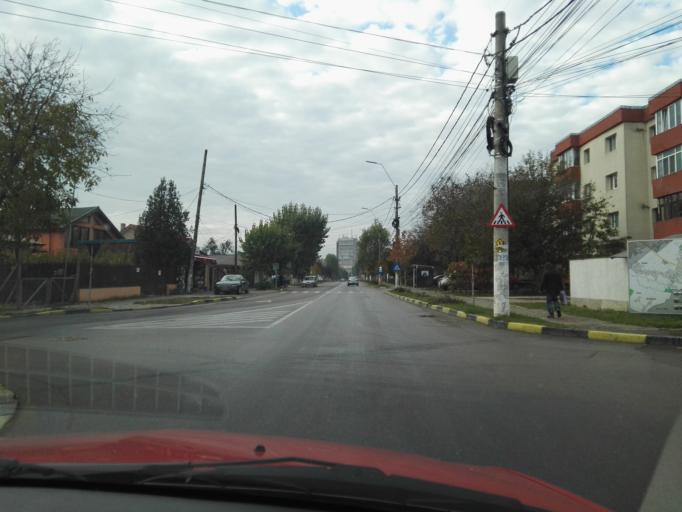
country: RO
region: Ilfov
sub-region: Comuna Magurele
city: Magurele
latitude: 44.3544
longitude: 26.0336
